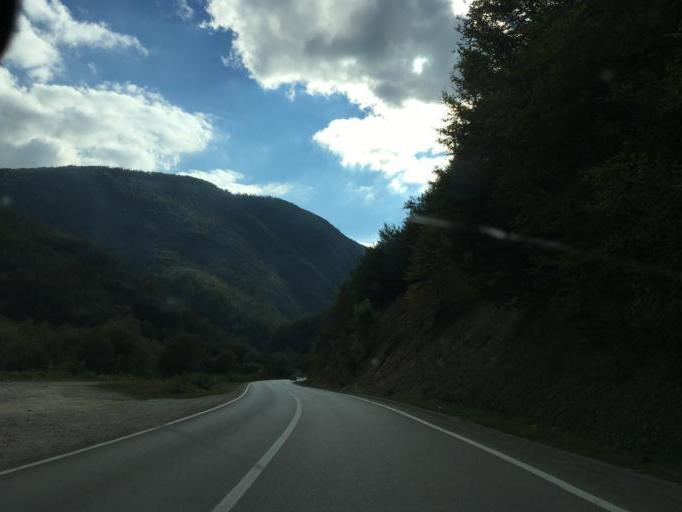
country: BA
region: Federation of Bosnia and Herzegovina
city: Bugojno
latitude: 44.0919
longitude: 17.5549
